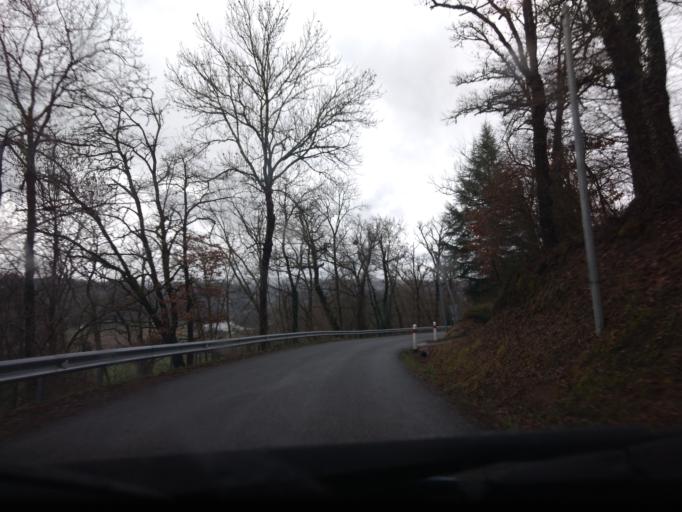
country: FR
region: Midi-Pyrenees
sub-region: Departement de l'Aveyron
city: Livinhac-le-Haut
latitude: 44.6042
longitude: 2.2298
